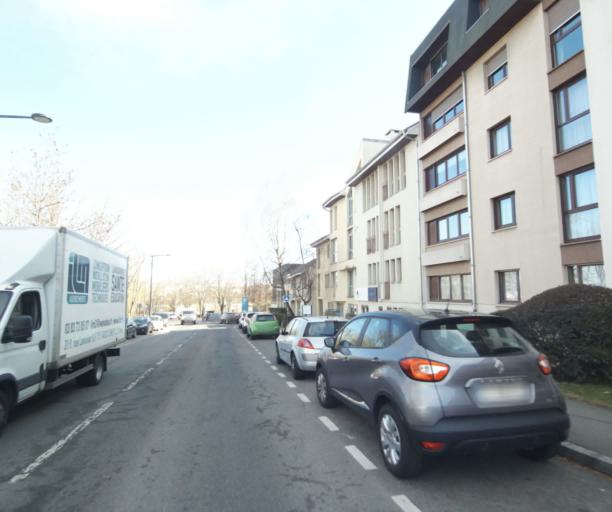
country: FR
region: Lorraine
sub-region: Departement de Meurthe-et-Moselle
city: Villers-les-Nancy
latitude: 48.6717
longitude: 6.1522
